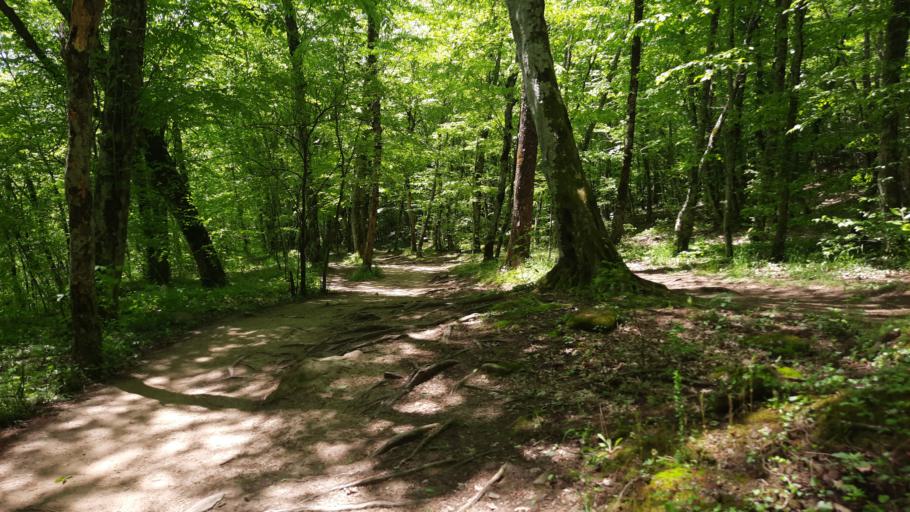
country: RU
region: Krasnodarskiy
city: Divnomorskoye
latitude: 44.5565
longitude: 38.2522
